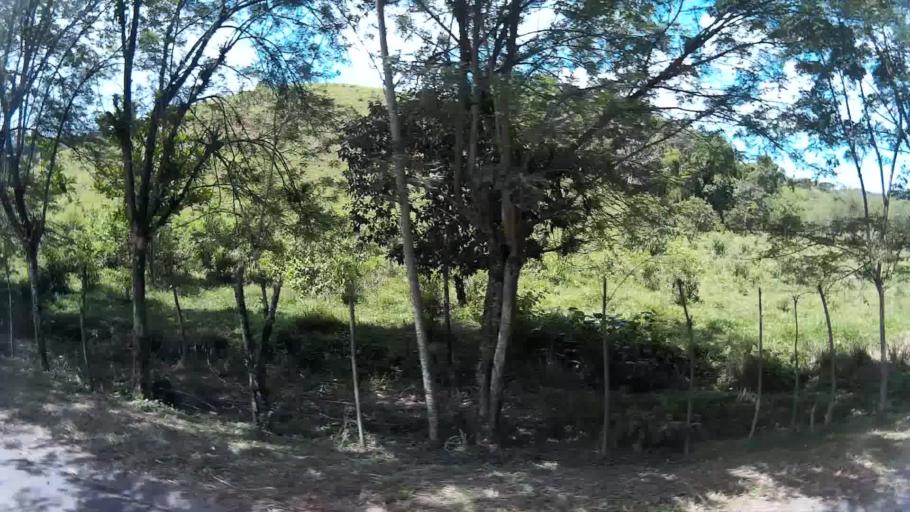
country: CO
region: Risaralda
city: La Virginia
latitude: 4.9221
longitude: -75.8656
